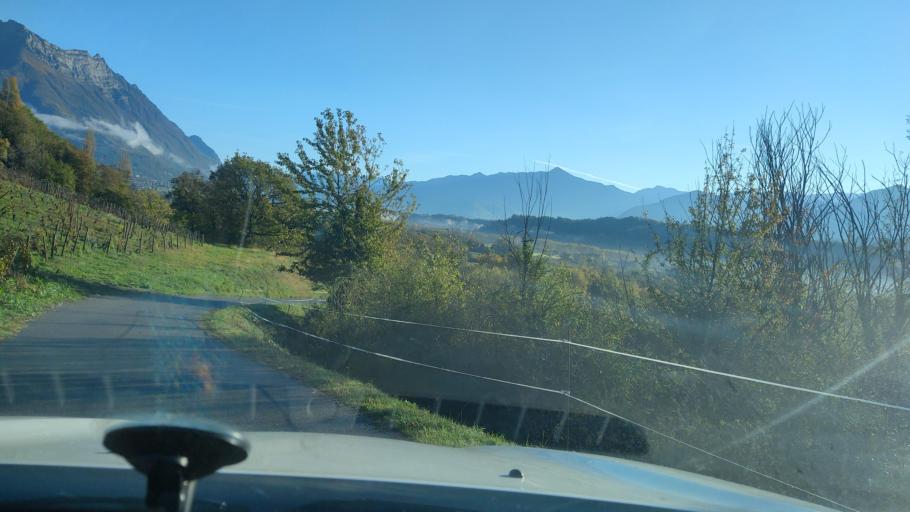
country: FR
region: Rhone-Alpes
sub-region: Departement de la Savoie
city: Cruet
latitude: 45.5333
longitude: 6.1056
